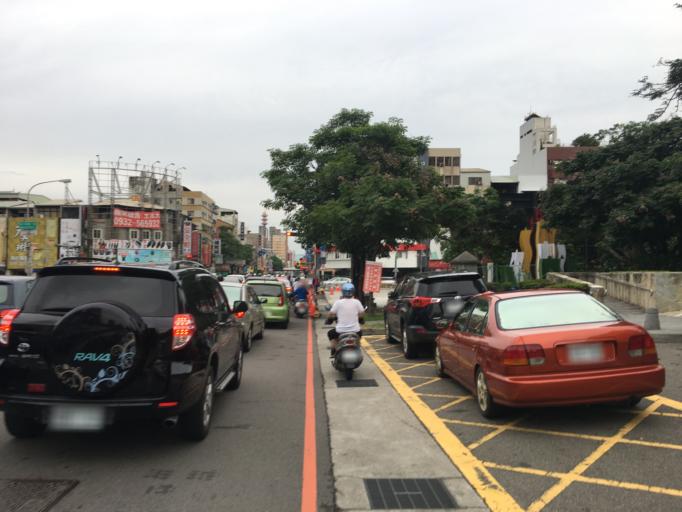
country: TW
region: Taiwan
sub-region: Taichung City
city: Taichung
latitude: 24.1416
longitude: 120.6661
